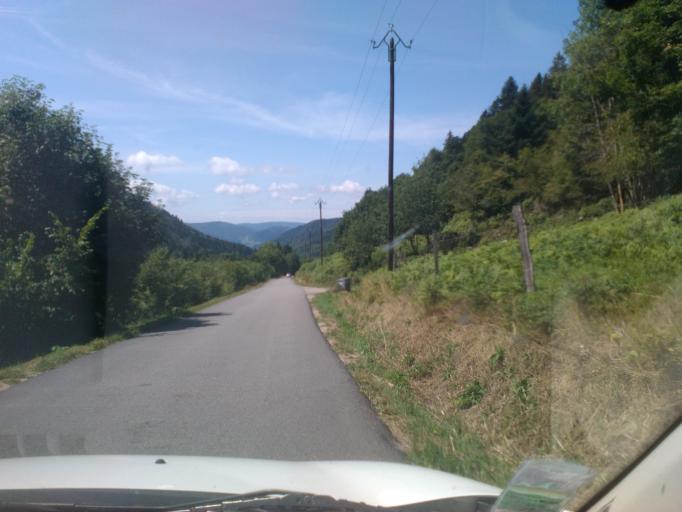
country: FR
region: Lorraine
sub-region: Departement des Vosges
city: La Bresse
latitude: 48.0383
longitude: 6.8171
